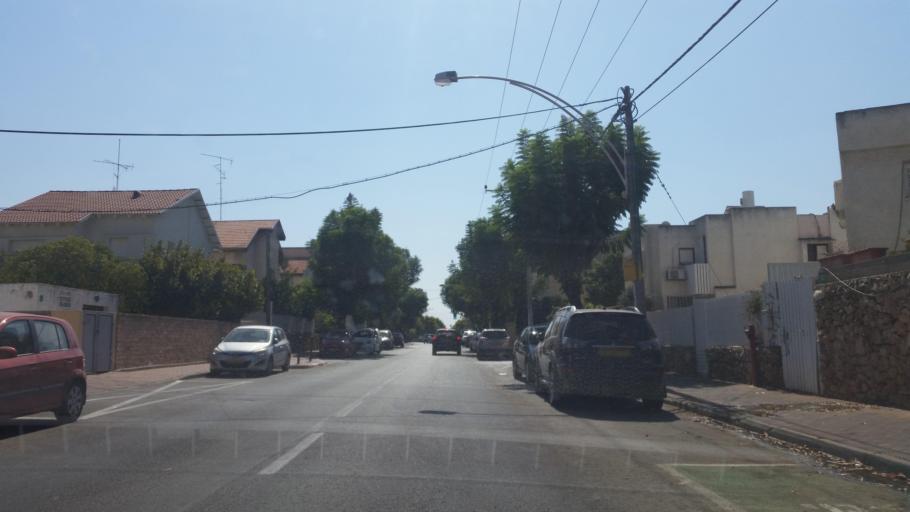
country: IL
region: Central District
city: Ra'anana
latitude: 32.1797
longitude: 34.8848
